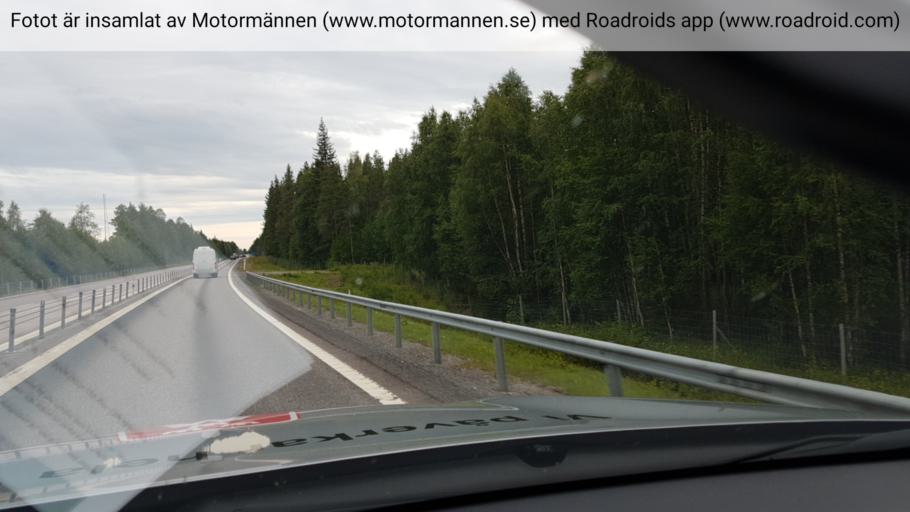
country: SE
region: Norrbotten
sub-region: Lulea Kommun
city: Ranea
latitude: 65.7909
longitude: 22.1810
